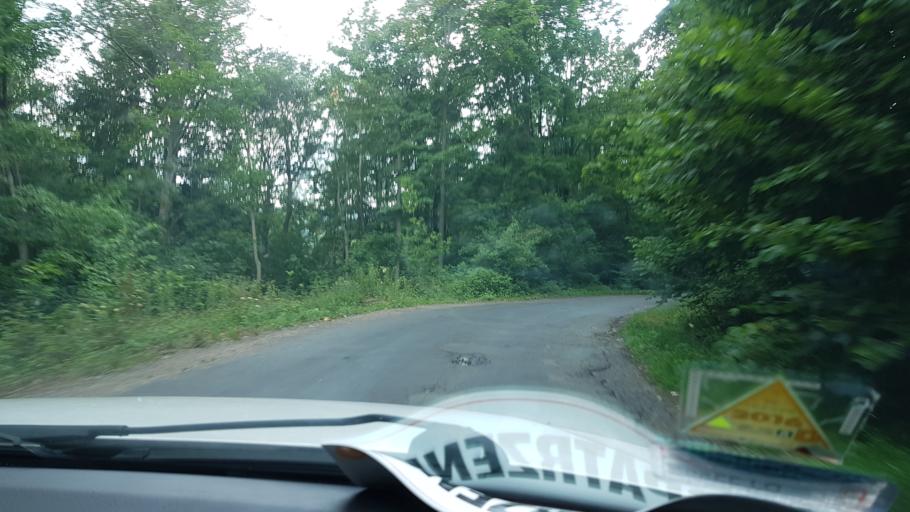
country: PL
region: Lower Silesian Voivodeship
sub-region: Powiat jeleniogorski
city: Jezow Sudecki
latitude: 50.9700
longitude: 15.8143
